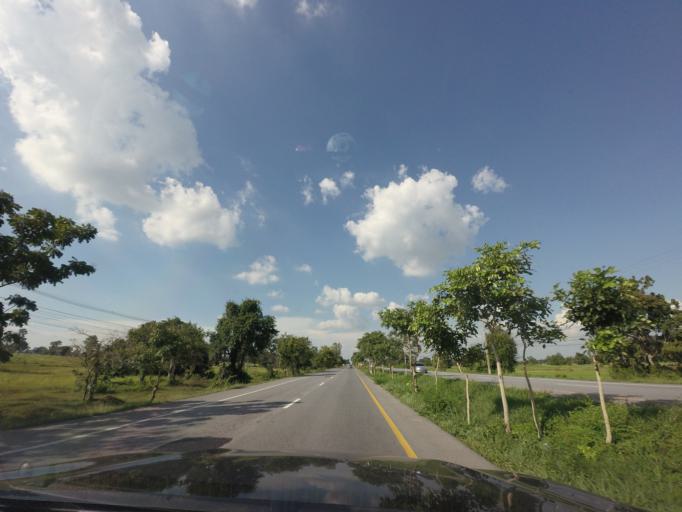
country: TH
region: Khon Kaen
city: Phon
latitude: 15.7161
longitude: 102.5898
